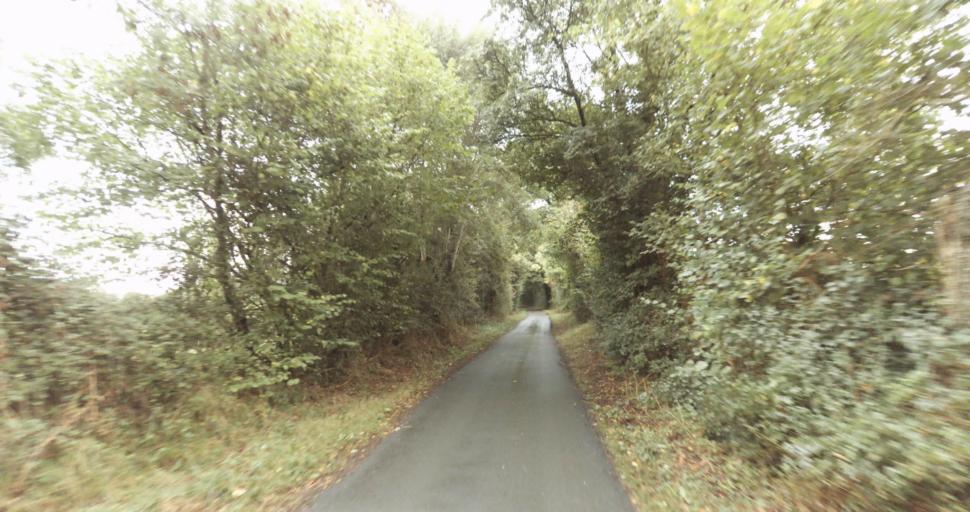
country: FR
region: Lower Normandy
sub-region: Departement de l'Orne
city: Vimoutiers
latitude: 48.9095
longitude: 0.1684
